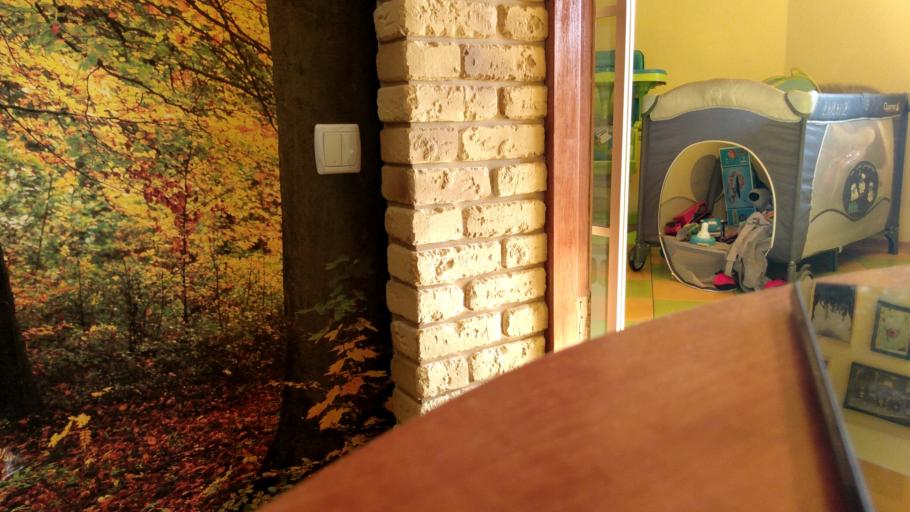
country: RU
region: Tverskaya
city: Radchenko
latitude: 56.6782
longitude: 36.4598
